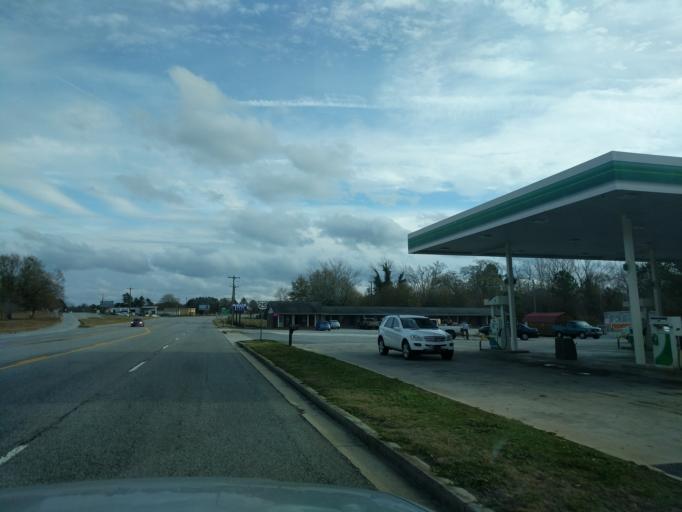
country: US
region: South Carolina
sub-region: Greenwood County
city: Ware Shoals
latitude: 34.5028
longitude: -82.2924
